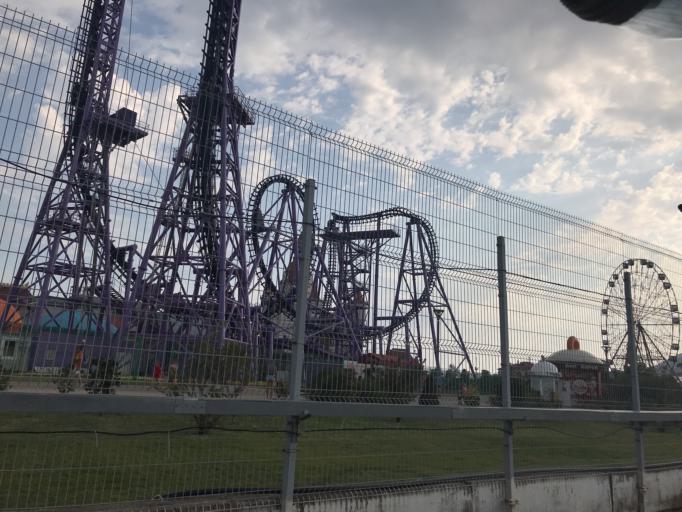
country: RU
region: Krasnodarskiy
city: Adler
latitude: 43.4060
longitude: 39.9649
